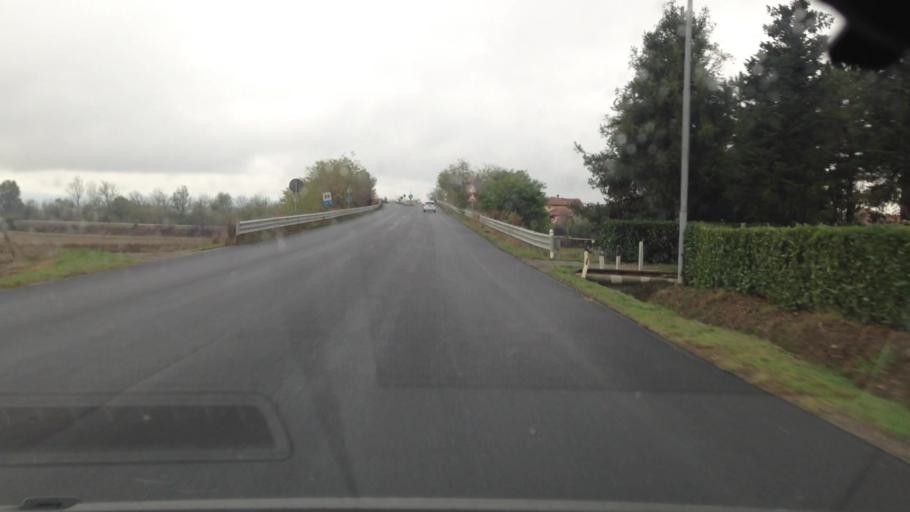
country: IT
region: Piedmont
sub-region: Provincia di Asti
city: Villanova d'Asti
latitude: 44.9623
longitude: 7.9085
